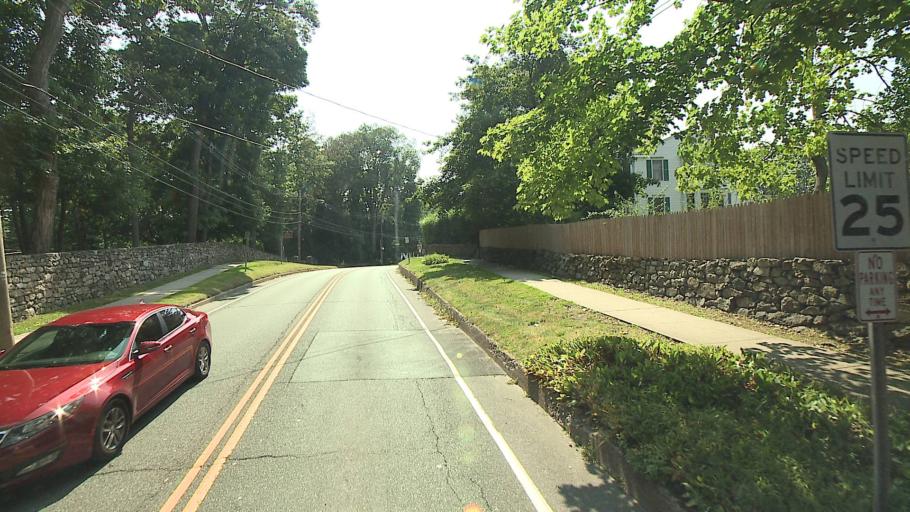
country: US
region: Connecticut
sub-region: Fairfield County
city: Ridgefield
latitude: 41.2871
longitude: -73.4994
